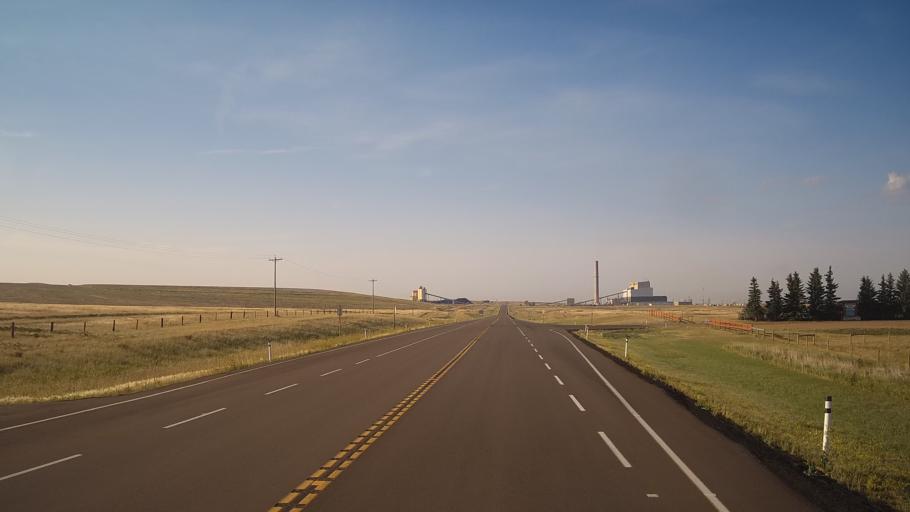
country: CA
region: Alberta
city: Hanna
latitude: 51.4628
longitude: -111.7869
